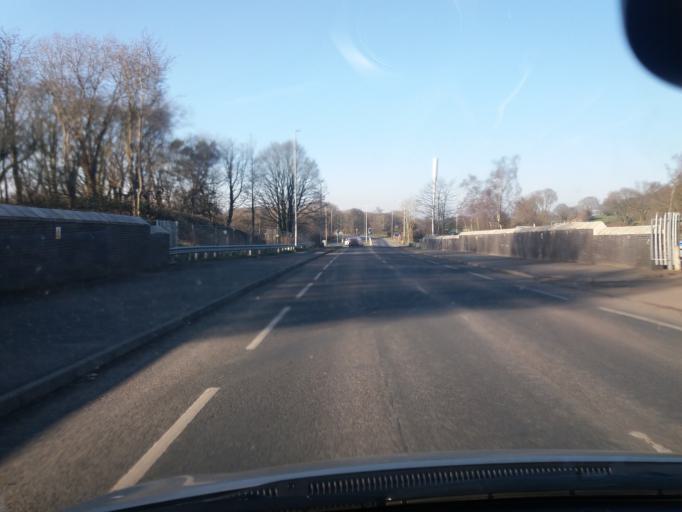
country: GB
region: England
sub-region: Lancashire
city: Adlington
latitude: 53.6274
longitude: -2.6089
